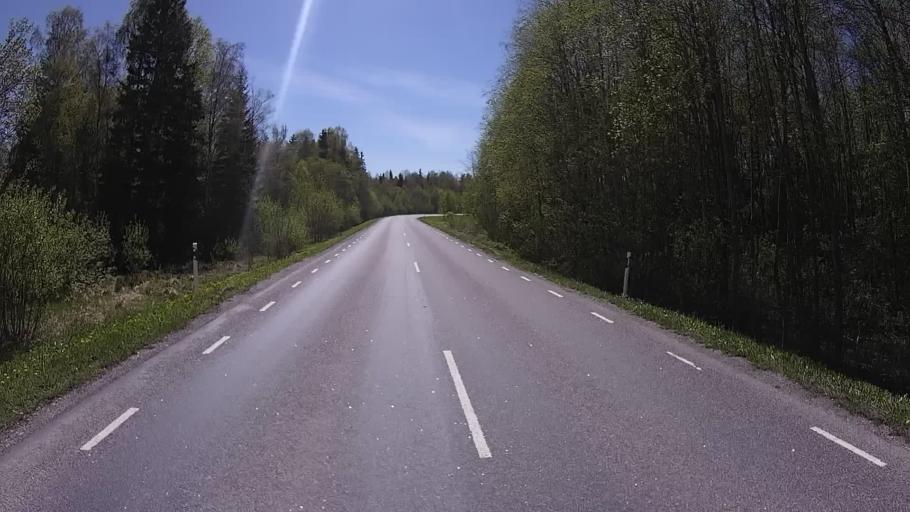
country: EE
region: Harju
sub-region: Raasiku vald
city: Raasiku
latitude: 59.0849
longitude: 25.1762
